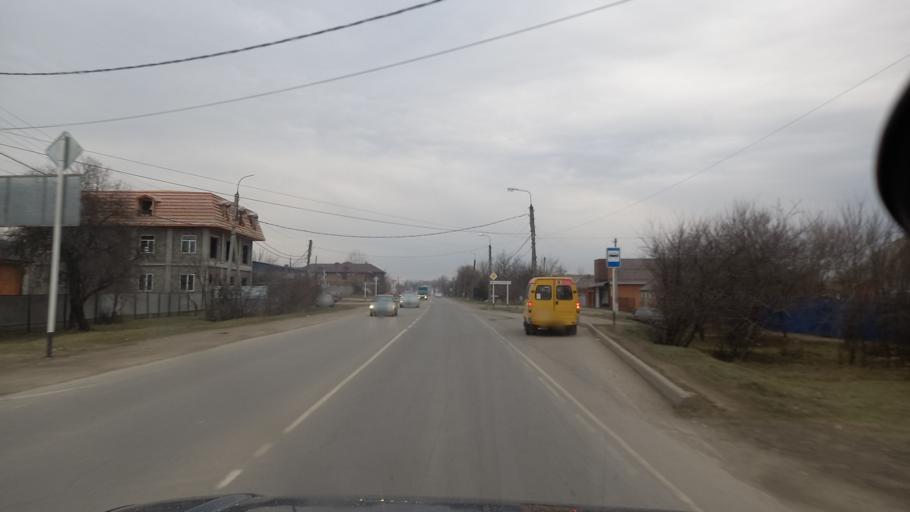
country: RU
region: Adygeya
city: Maykop
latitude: 44.5855
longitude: 40.1331
